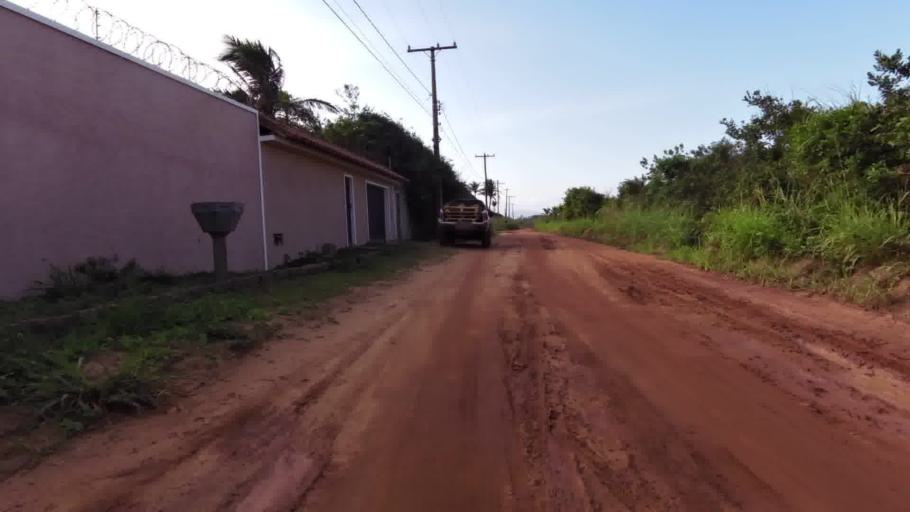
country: BR
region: Espirito Santo
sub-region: Piuma
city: Piuma
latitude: -20.8207
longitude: -40.6155
